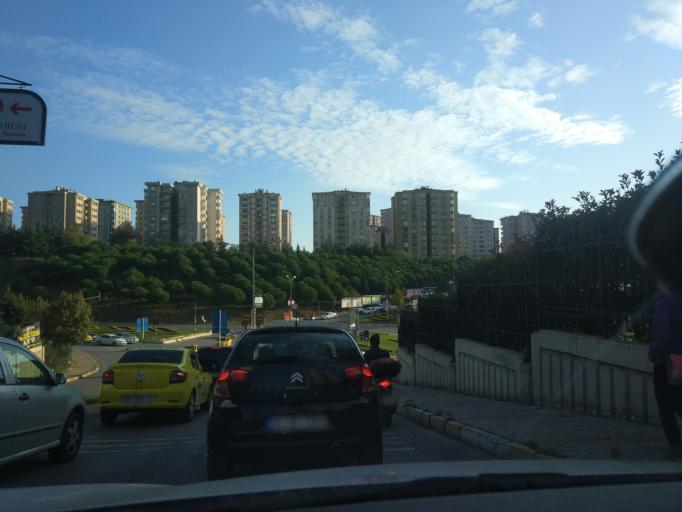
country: TR
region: Istanbul
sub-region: Atasehir
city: Atasehir
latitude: 40.9890
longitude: 29.1254
